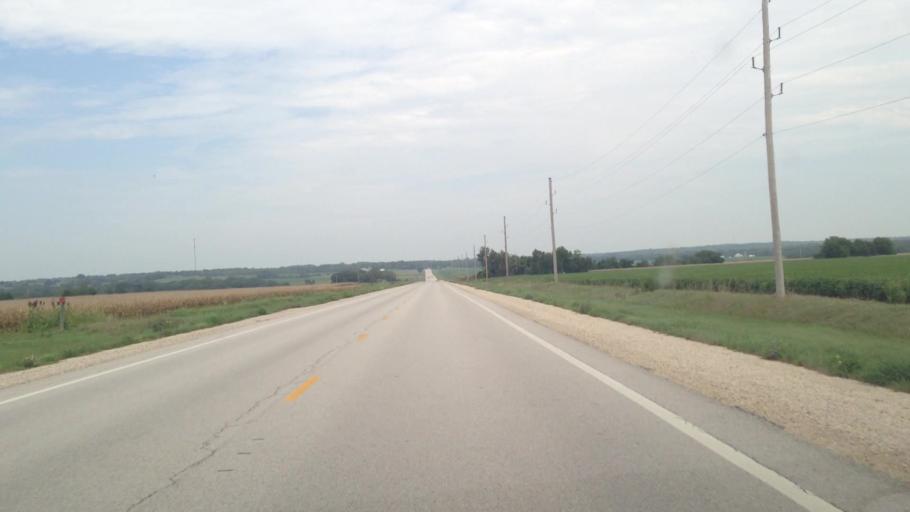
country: US
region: Kansas
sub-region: Anderson County
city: Garnett
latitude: 38.0589
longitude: -95.1693
